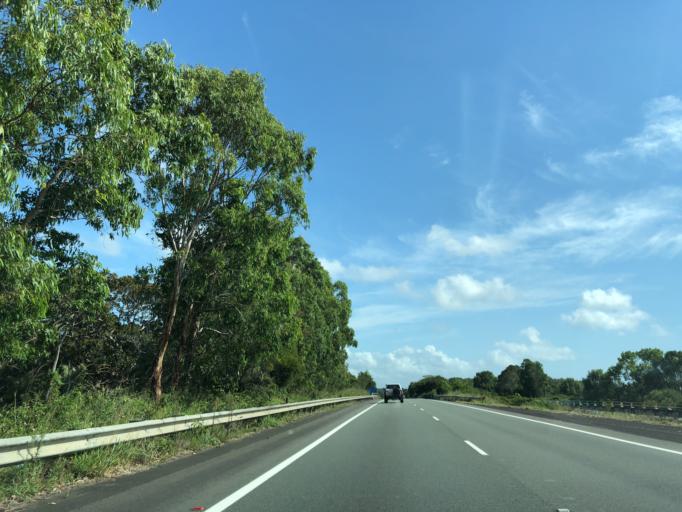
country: AU
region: New South Wales
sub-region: Byron Shire
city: Brunswick Heads
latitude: -28.6055
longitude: 153.5460
